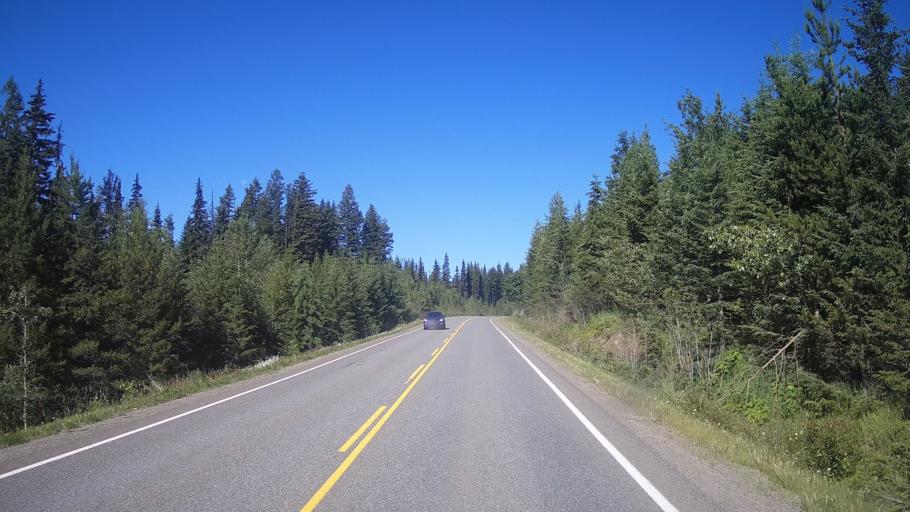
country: CA
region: British Columbia
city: Kamloops
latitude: 51.4969
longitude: -120.4265
